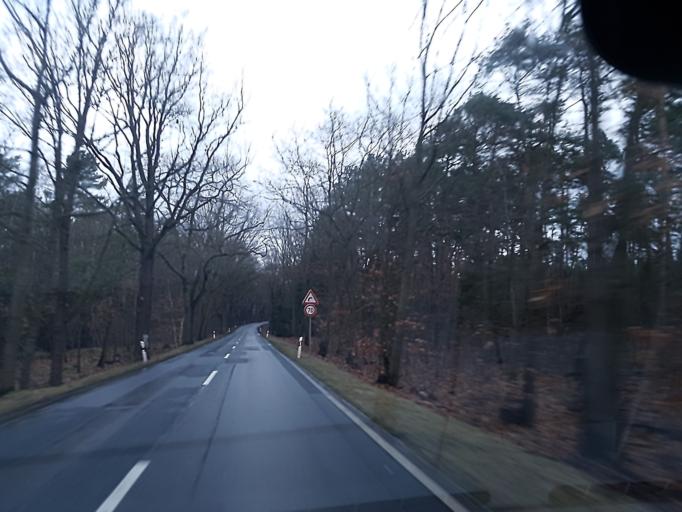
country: DE
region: Brandenburg
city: Hohenleipisch
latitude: 51.5097
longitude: 13.5630
